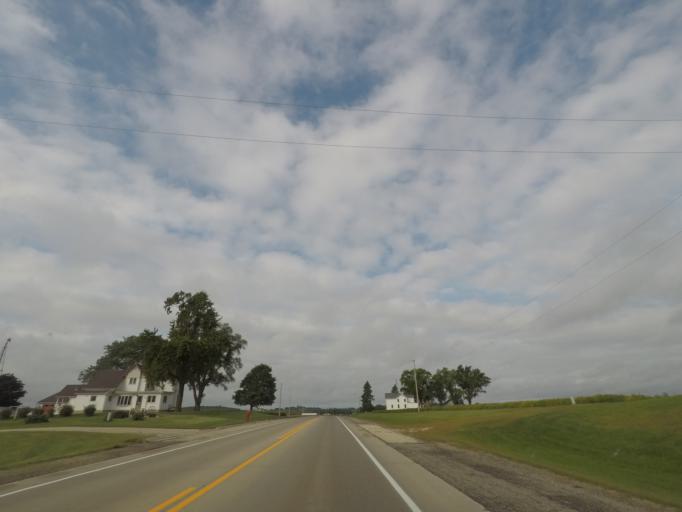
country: US
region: Wisconsin
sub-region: Dane County
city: Cottage Grove
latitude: 43.0303
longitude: -89.1532
